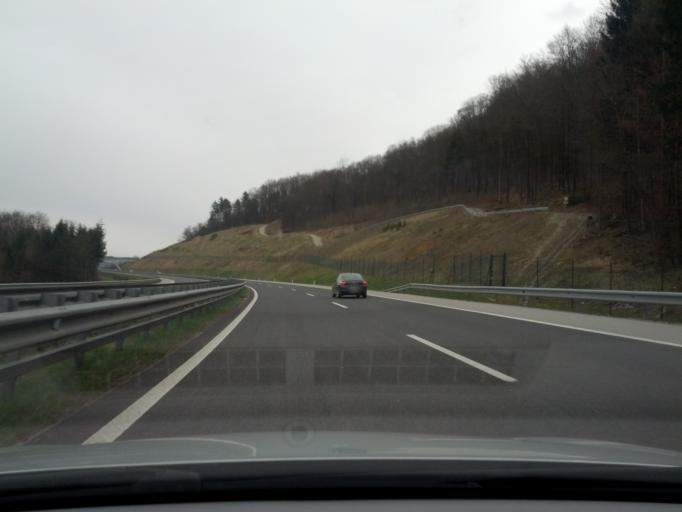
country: SI
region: Trebnje
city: Trebnje
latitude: 45.9016
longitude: 14.9972
